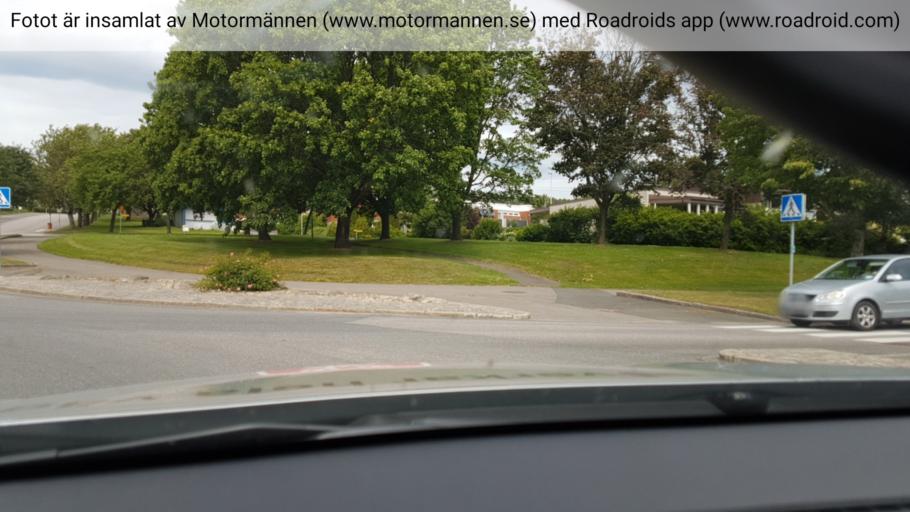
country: SE
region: Vaestra Goetaland
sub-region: Falkopings Kommun
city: Falkoeping
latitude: 58.1676
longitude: 13.5359
